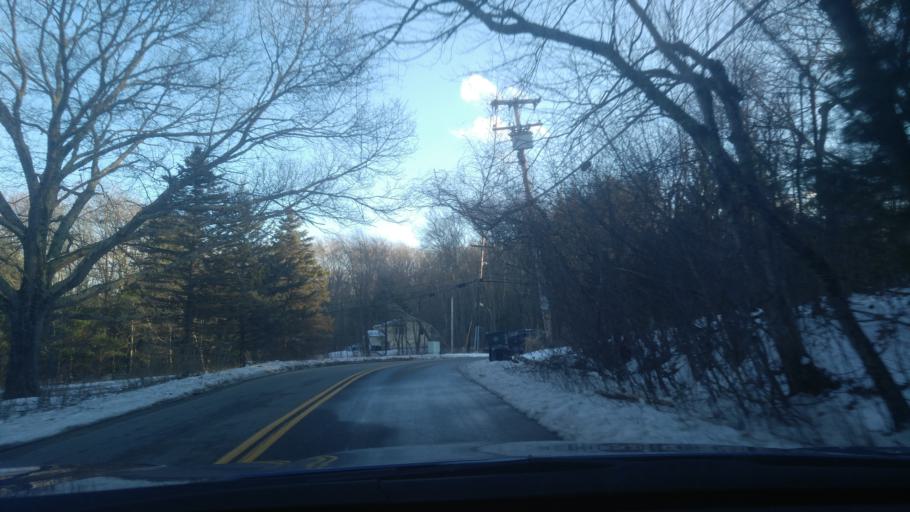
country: US
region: Rhode Island
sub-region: Kent County
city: Coventry
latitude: 41.7115
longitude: -71.6505
